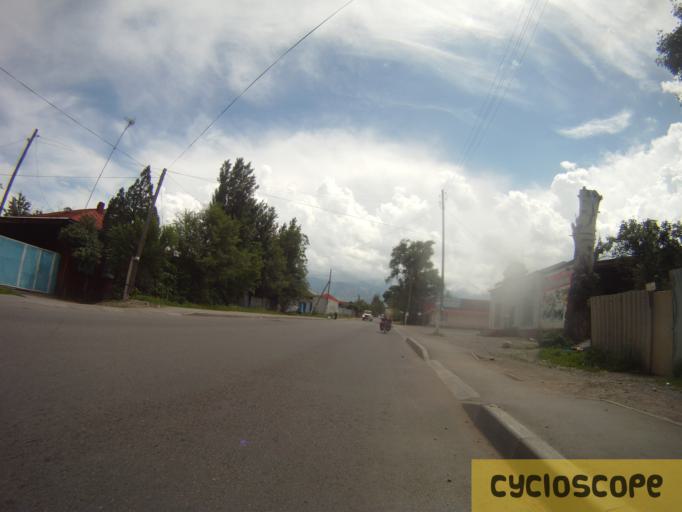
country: KZ
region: Almaty Oblysy
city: Esik
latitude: 43.3495
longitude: 77.4696
